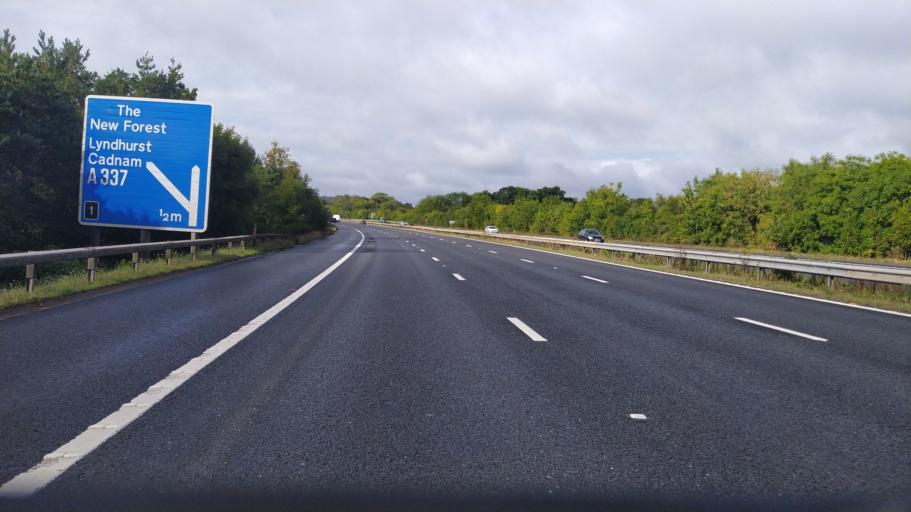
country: GB
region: England
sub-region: Hampshire
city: Cadnam
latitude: 50.9284
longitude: -1.5739
